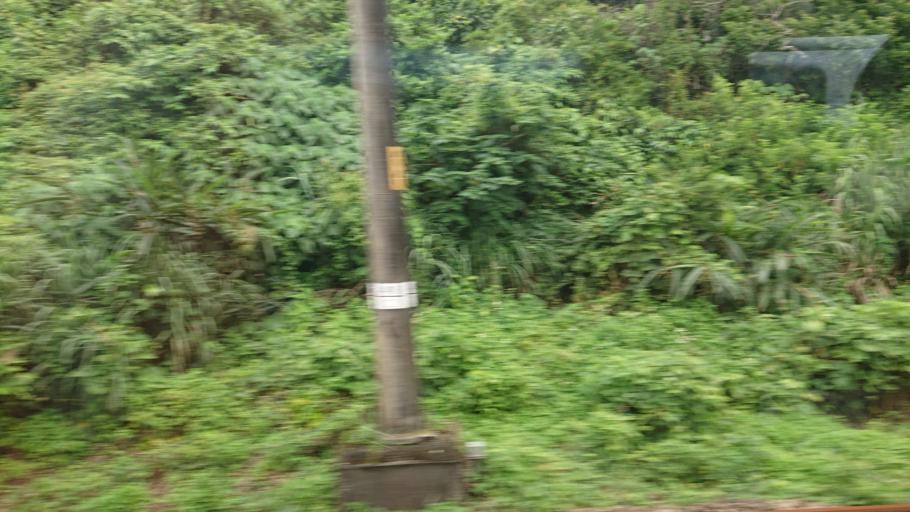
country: TW
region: Taiwan
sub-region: Yilan
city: Yilan
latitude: 24.9137
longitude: 121.8780
